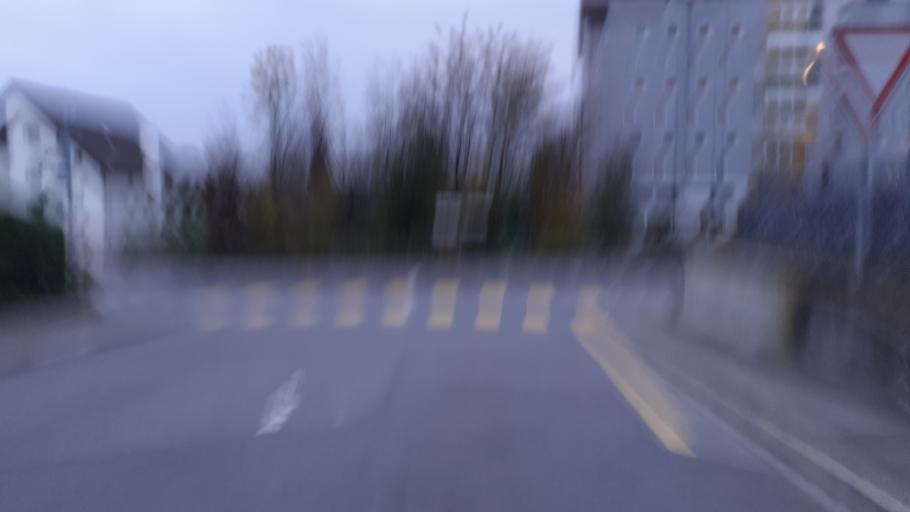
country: CH
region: Saint Gallen
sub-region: Wahlkreis Rheintal
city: Altstatten
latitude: 47.3764
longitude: 9.5542
